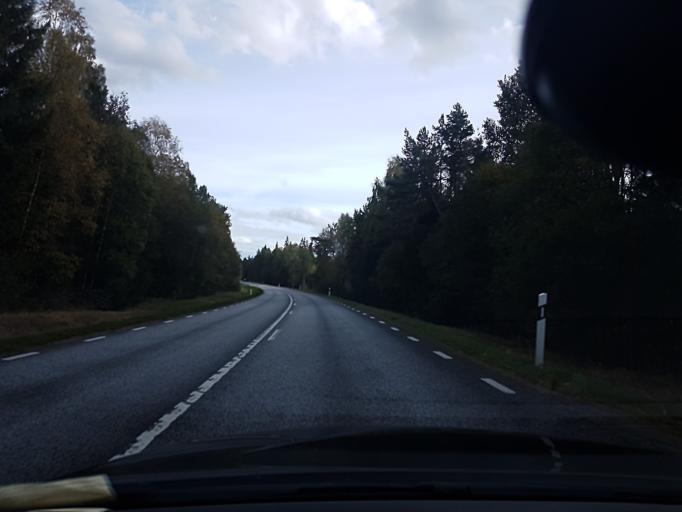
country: SE
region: Joenkoeping
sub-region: Varnamo Kommun
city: Bredaryd
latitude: 57.1883
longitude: 13.7260
